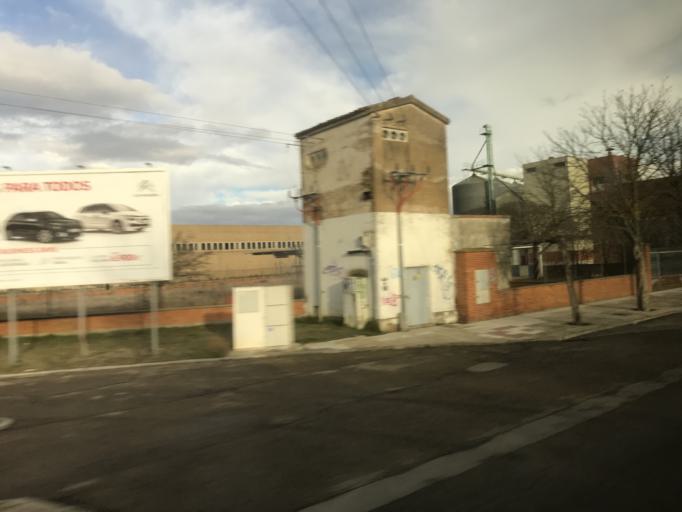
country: ES
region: Castille and Leon
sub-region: Provincia de Palencia
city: Palencia
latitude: 42.0257
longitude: -4.5491
